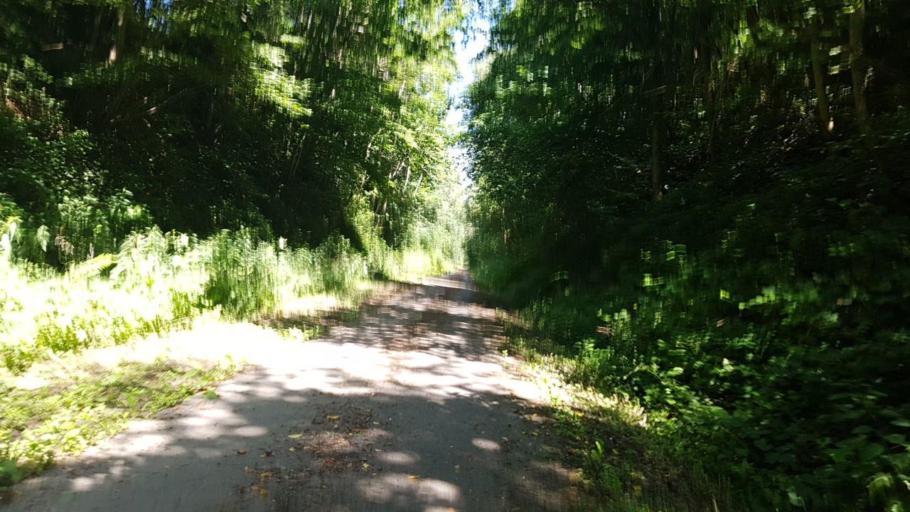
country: BE
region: Wallonia
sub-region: Province du Hainaut
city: Beaumont
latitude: 50.1958
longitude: 4.2254
